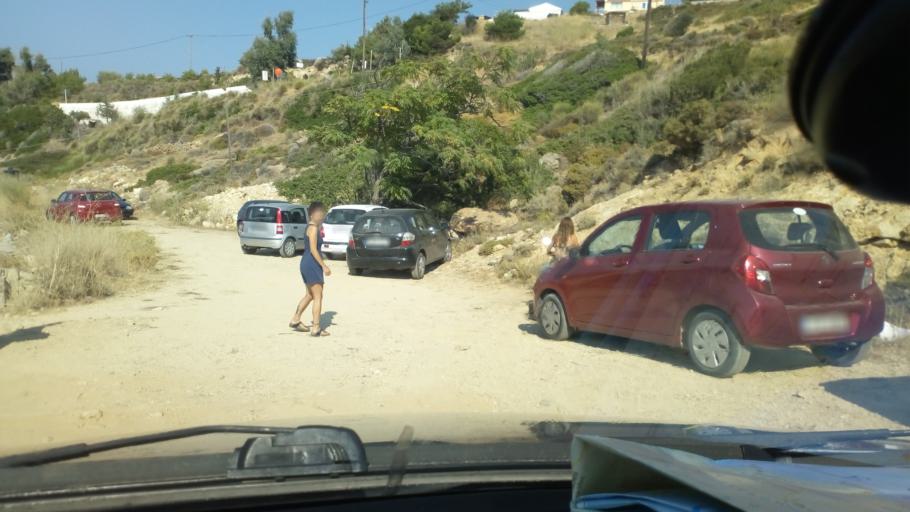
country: GR
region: North Aegean
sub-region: Nomos Samou
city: Agios Kirykos
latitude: 37.6298
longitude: 26.0916
